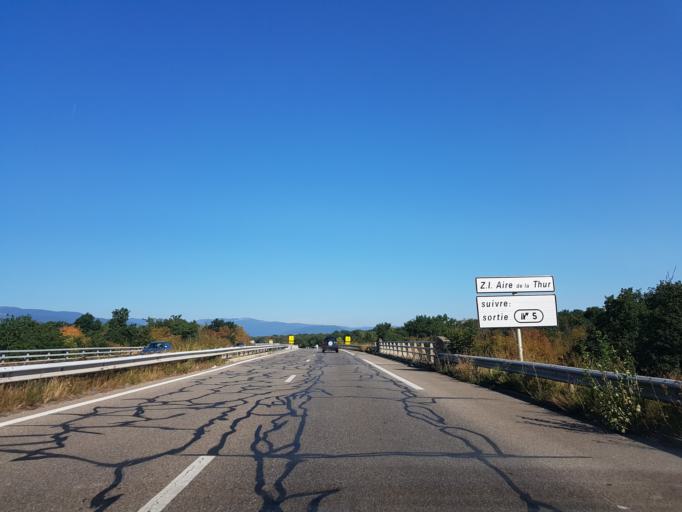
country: FR
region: Alsace
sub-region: Departement du Haut-Rhin
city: Pulversheim
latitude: 47.8138
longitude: 7.2984
